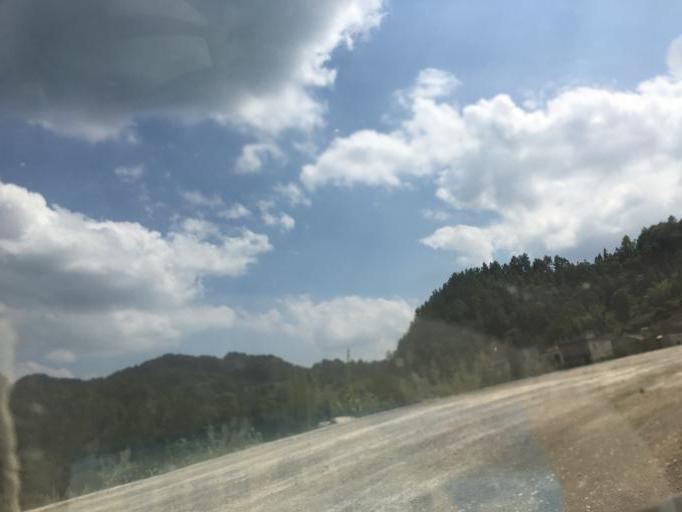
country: CN
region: Guizhou Sheng
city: Fuxing
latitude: 28.0694
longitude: 107.9123
